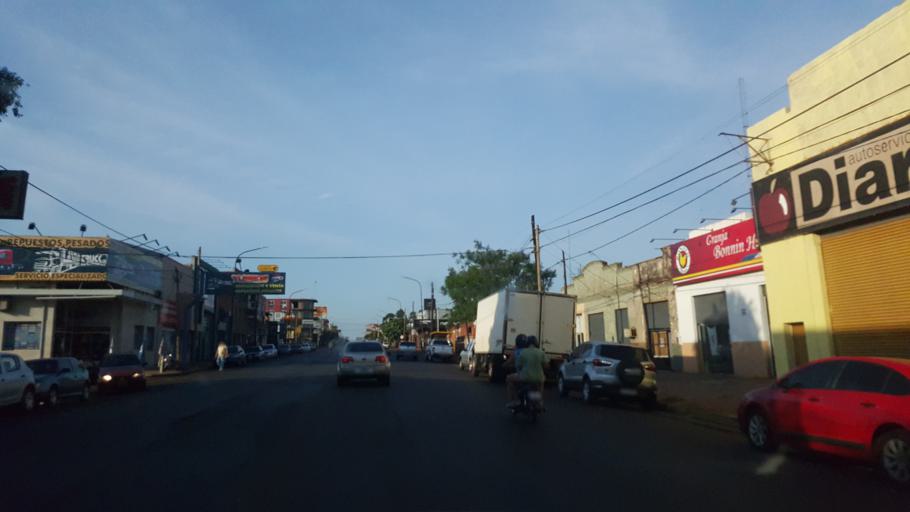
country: AR
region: Misiones
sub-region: Departamento de Capital
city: Posadas
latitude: -27.4031
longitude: -55.9025
